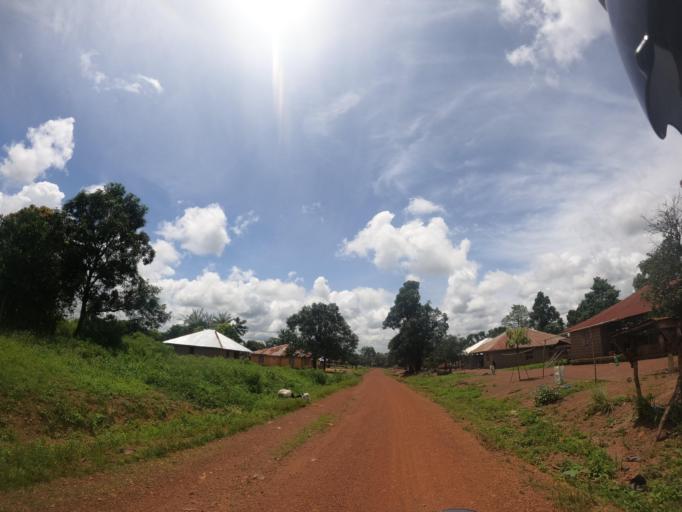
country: SL
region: Northern Province
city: Makeni
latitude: 9.1254
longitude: -12.2555
